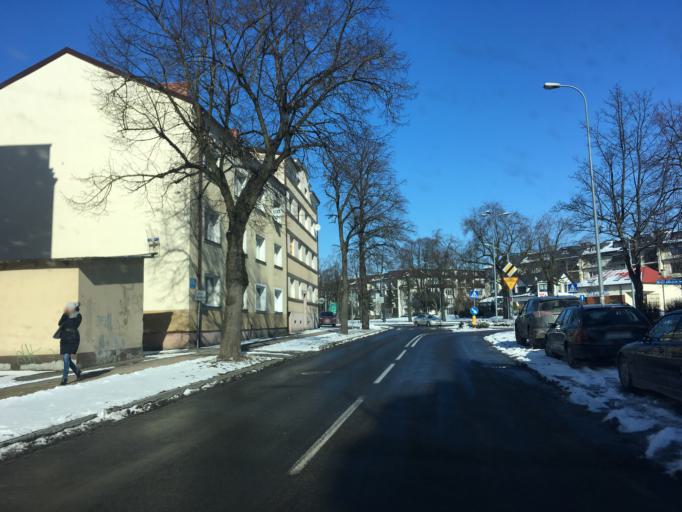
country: PL
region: Pomeranian Voivodeship
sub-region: Slupsk
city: Slupsk
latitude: 54.4621
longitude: 17.0417
